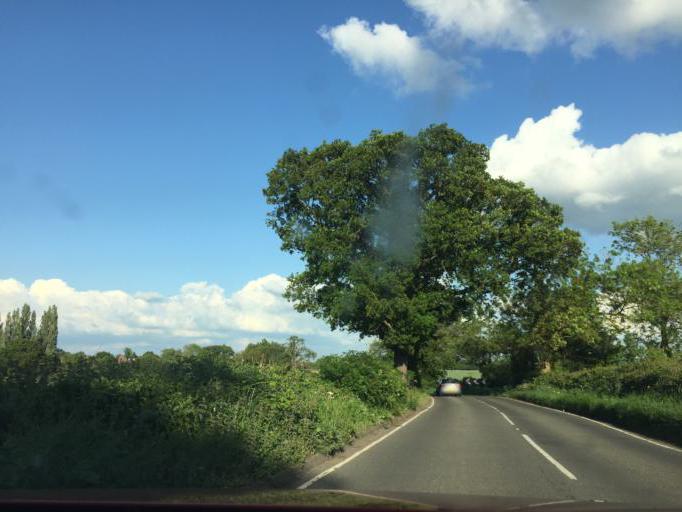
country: GB
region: England
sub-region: Warwickshire
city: Attleborough
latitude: 52.5002
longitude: -1.4550
